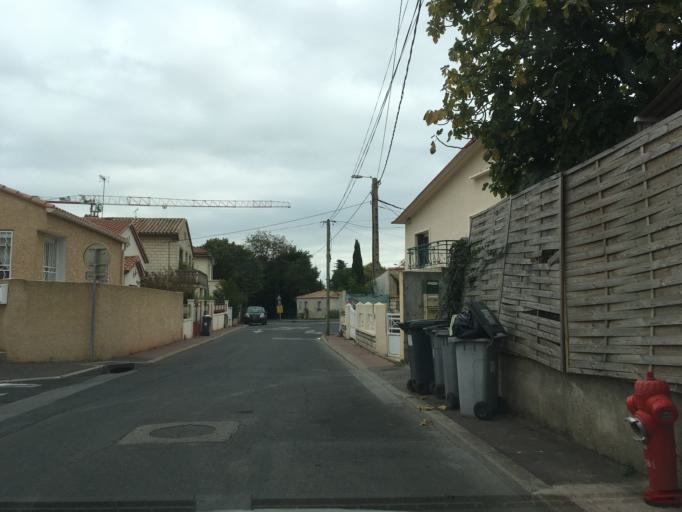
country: FR
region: Languedoc-Roussillon
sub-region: Departement de l'Herault
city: Montpellier
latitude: 43.5975
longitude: 3.8799
